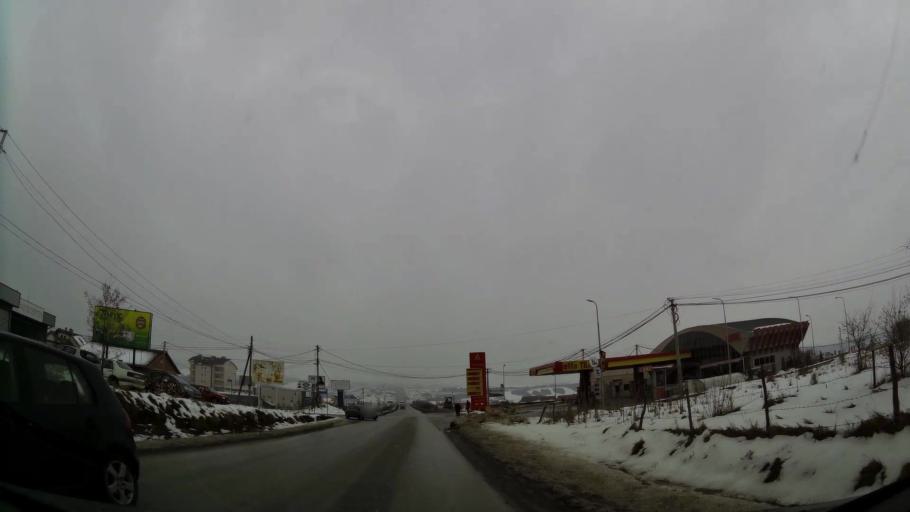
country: XK
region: Pristina
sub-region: Komuna e Prishtines
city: Pristina
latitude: 42.7131
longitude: 21.1510
